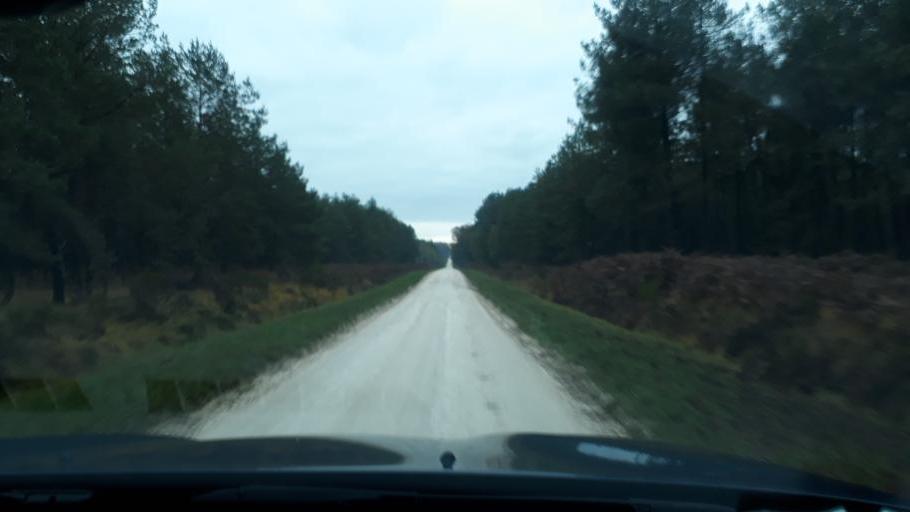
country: FR
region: Centre
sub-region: Departement du Loiret
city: Ouzouer-sur-Loire
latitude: 47.8381
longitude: 2.4559
